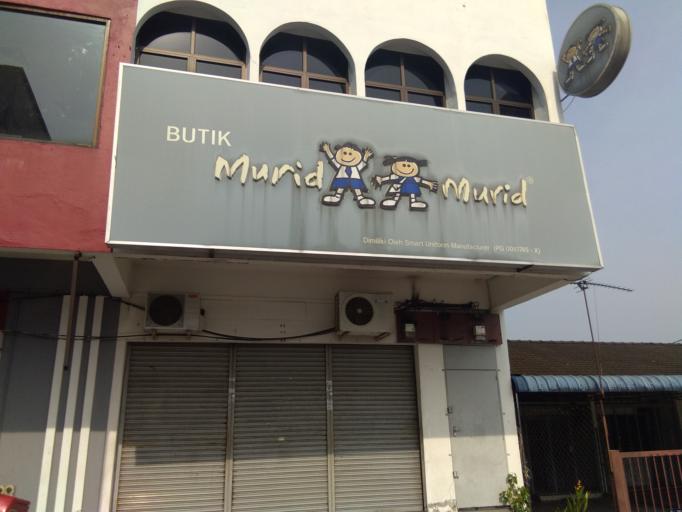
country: MY
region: Kedah
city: Kulim
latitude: 5.3722
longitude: 100.5544
